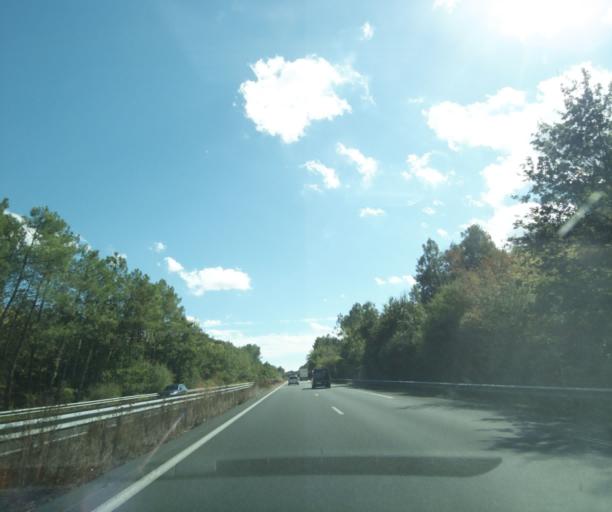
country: FR
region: Aquitaine
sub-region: Departement du Lot-et-Garonne
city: Fourques-sur-Garonne
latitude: 44.3978
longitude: 0.1912
